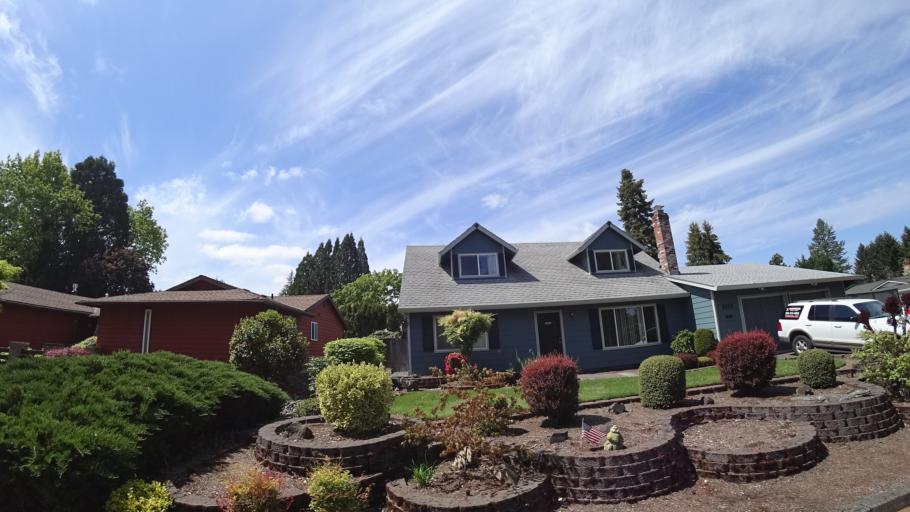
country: US
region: Oregon
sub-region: Washington County
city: Aloha
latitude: 45.4794
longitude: -122.8925
